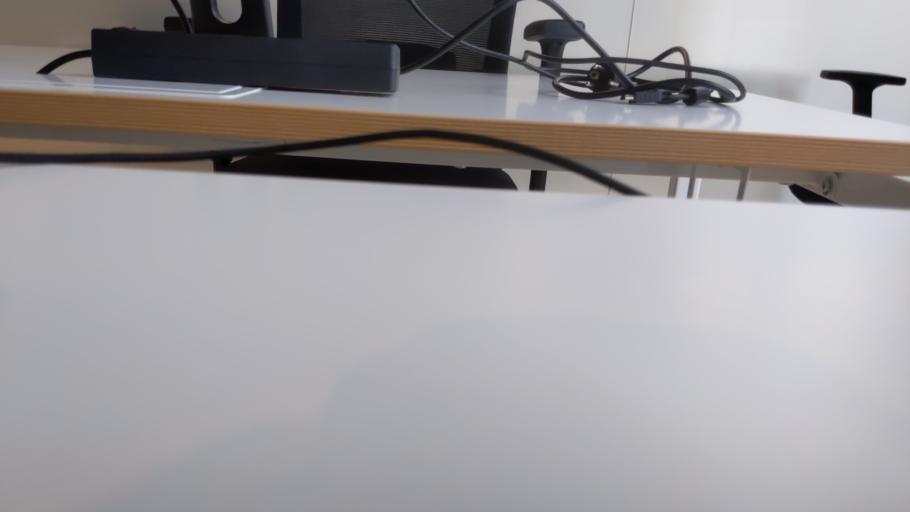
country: RU
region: Moskovskaya
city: Rogachevo
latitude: 56.4252
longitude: 37.1044
